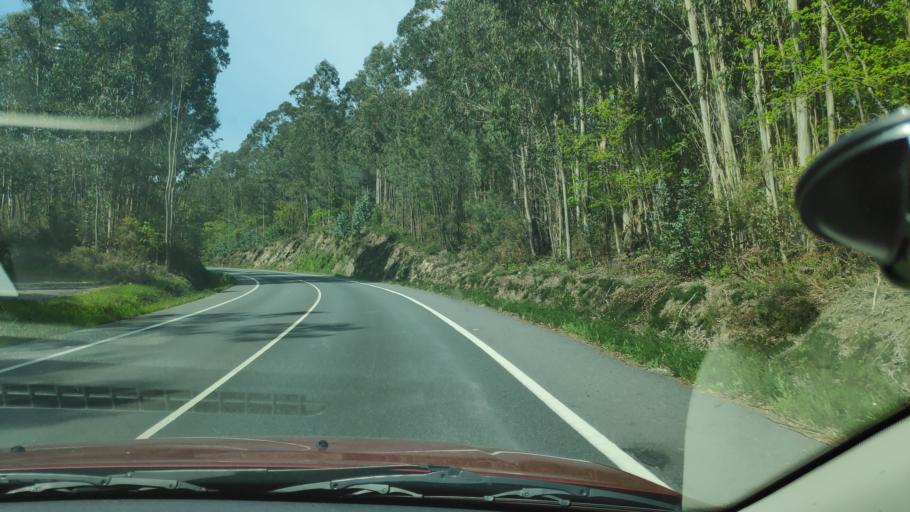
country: ES
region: Galicia
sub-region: Provincia da Coruna
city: Ames
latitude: 42.8744
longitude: -8.6591
